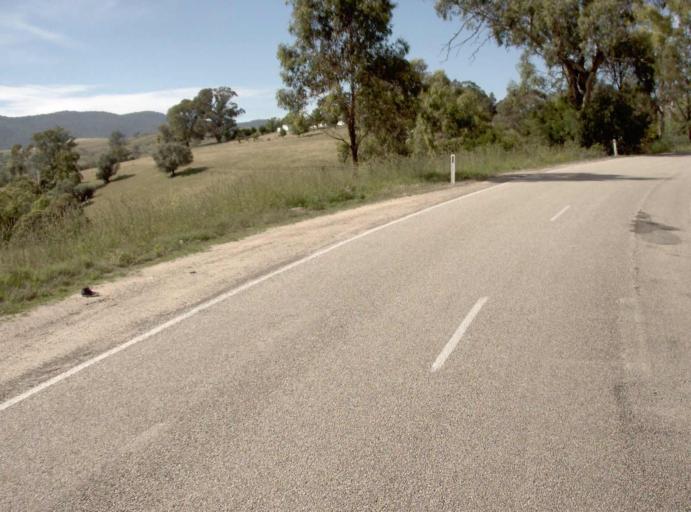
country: AU
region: Victoria
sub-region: East Gippsland
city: Lakes Entrance
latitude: -37.5121
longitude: 148.1678
